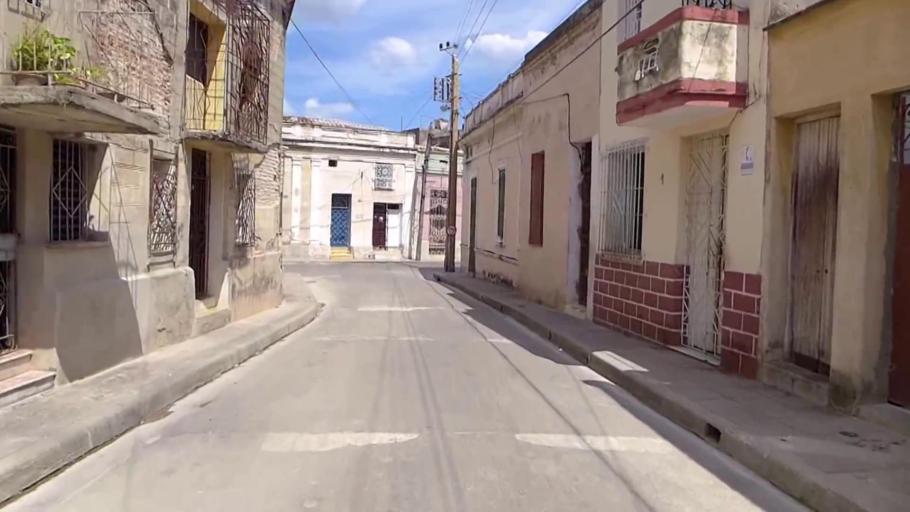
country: CU
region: Camaguey
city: Camaguey
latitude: 21.3808
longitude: -77.9182
